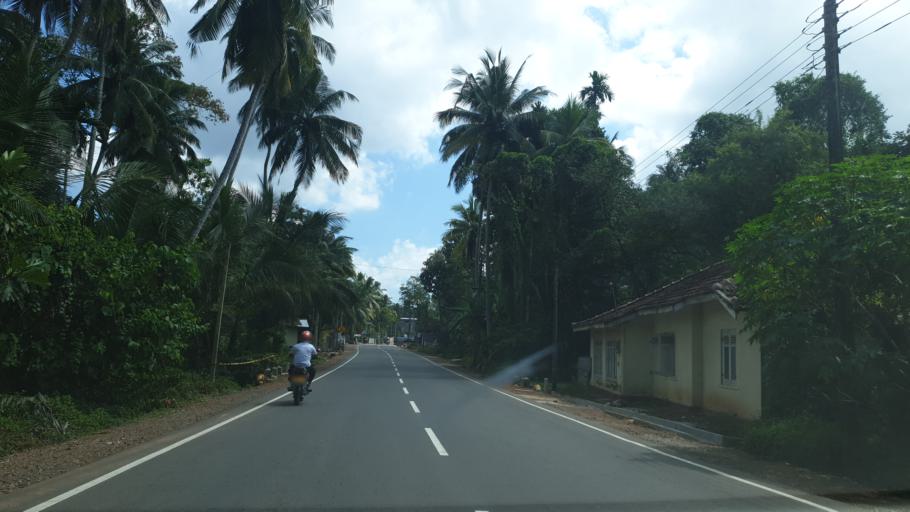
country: LK
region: Western
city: Panadura
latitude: 6.6699
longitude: 79.9427
